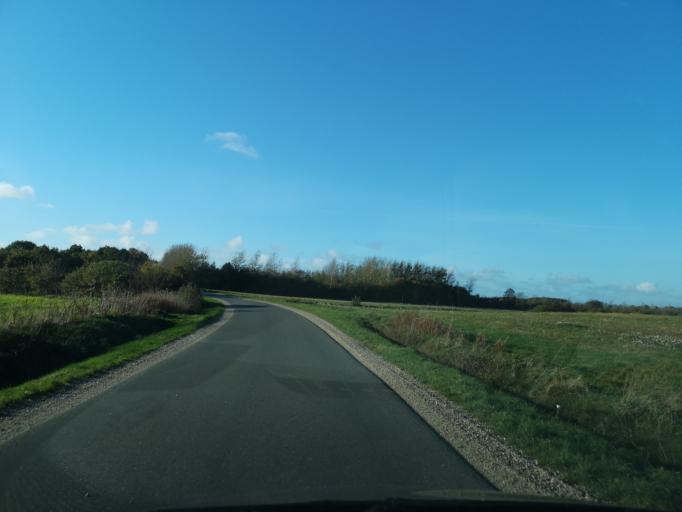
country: DK
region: Central Jutland
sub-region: Ringkobing-Skjern Kommune
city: Tarm
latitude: 55.8163
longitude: 8.4269
